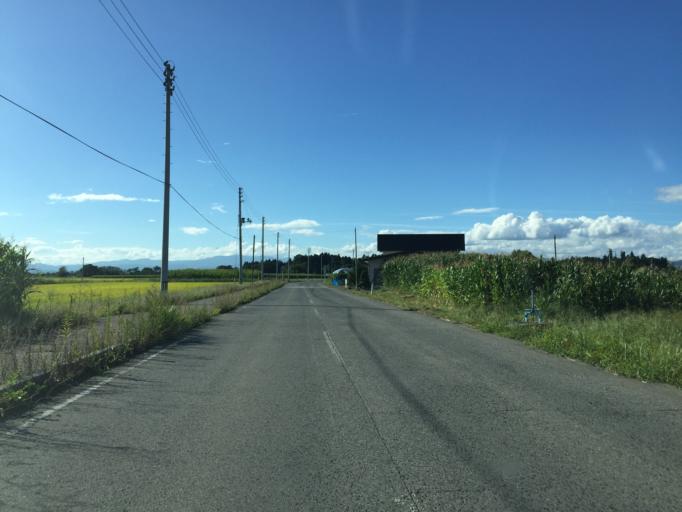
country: JP
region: Yamagata
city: Takahata
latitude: 37.9756
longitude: 140.1588
